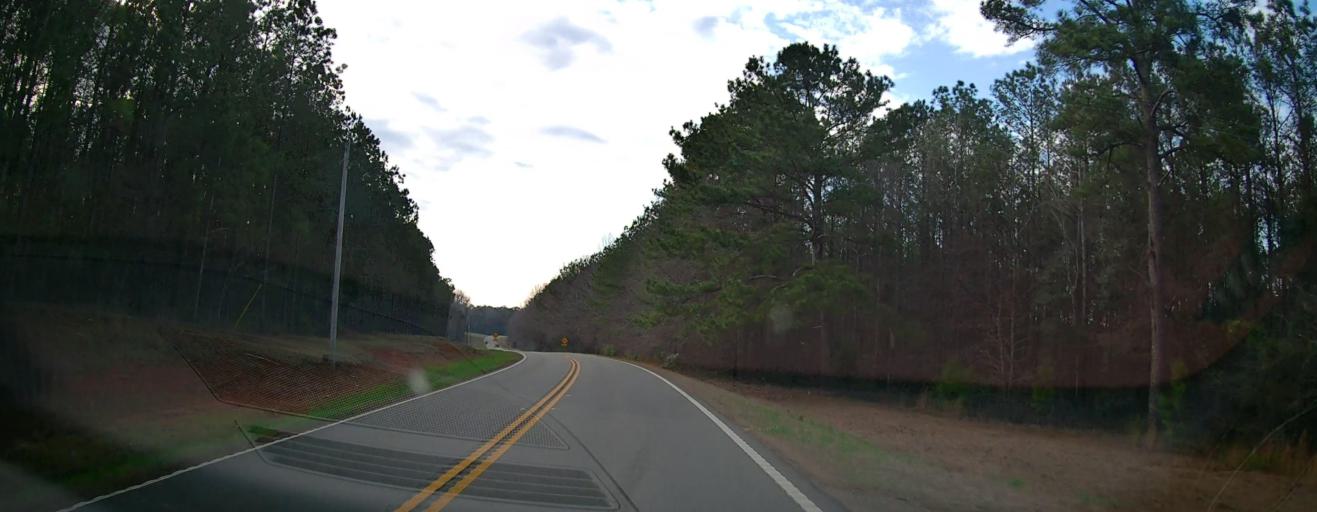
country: US
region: Georgia
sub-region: Harris County
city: Hamilton
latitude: 32.6973
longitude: -84.8028
